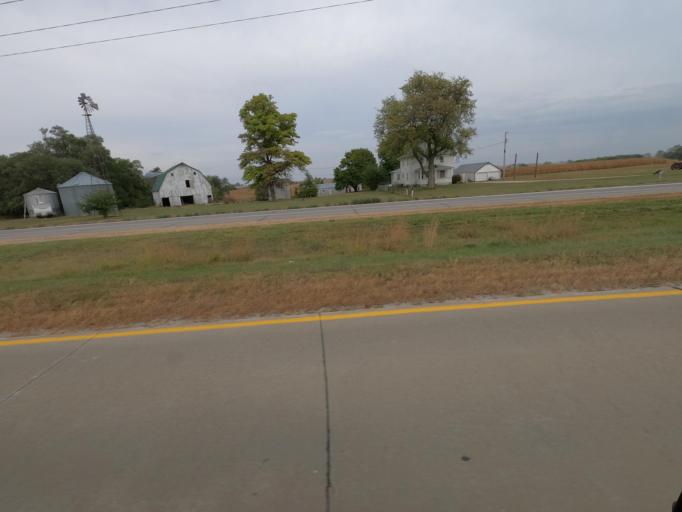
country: US
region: Iowa
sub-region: Marion County
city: Pella
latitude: 41.4293
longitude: -92.9837
